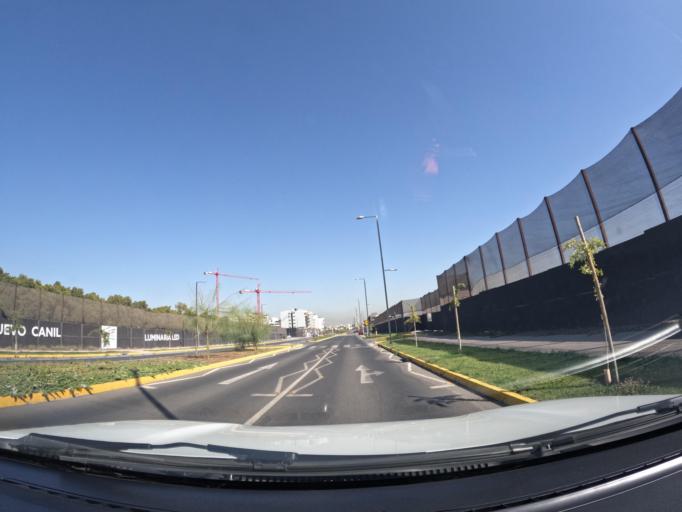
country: CL
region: Santiago Metropolitan
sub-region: Provincia de Santiago
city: Villa Presidente Frei, Nunoa, Santiago, Chile
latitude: -33.4863
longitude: -70.5704
